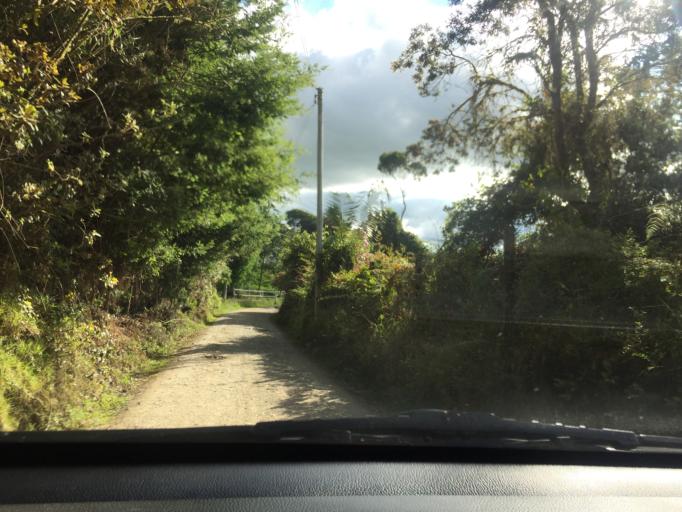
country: CO
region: Cundinamarca
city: Sopo
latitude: 4.9166
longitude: -73.9178
